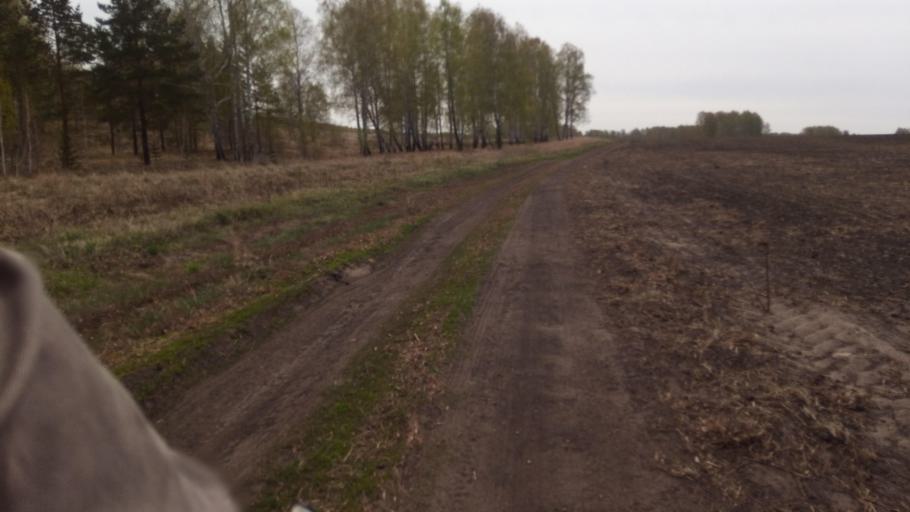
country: RU
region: Chelyabinsk
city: Timiryazevskiy
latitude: 55.0171
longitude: 60.8568
